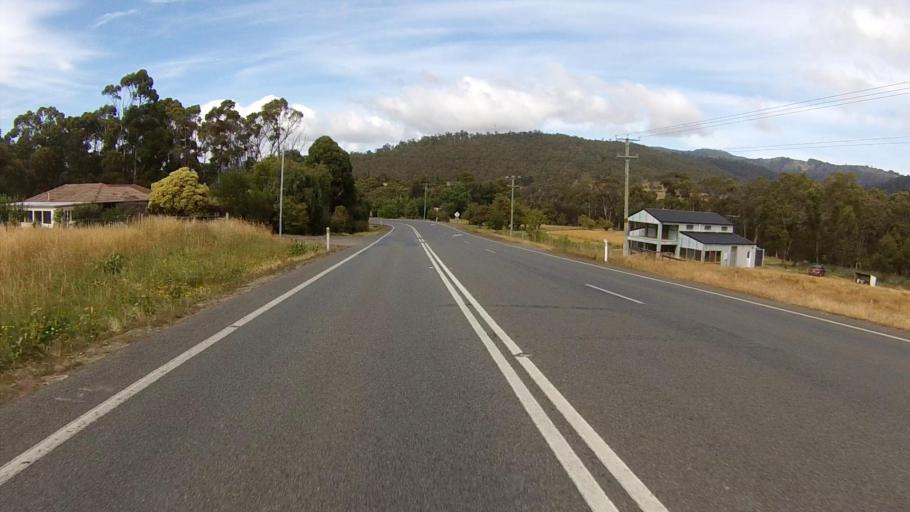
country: AU
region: Tasmania
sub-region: Kingborough
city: Kettering
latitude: -43.1175
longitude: 147.2443
